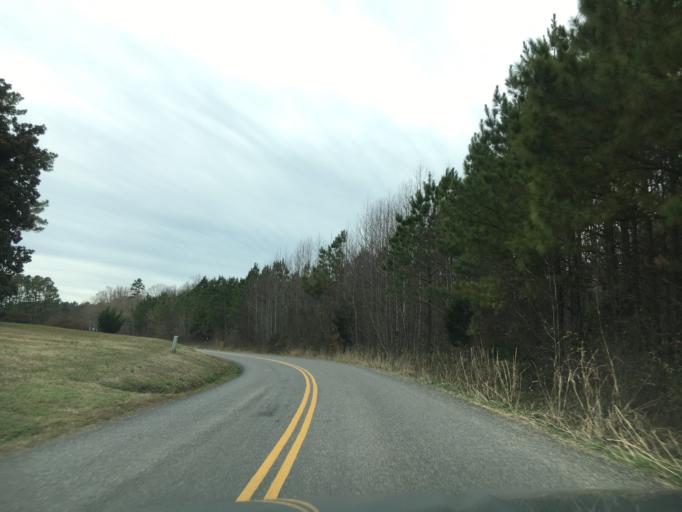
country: US
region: Virginia
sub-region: Amelia County
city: Amelia Court House
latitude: 37.4445
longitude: -78.0108
